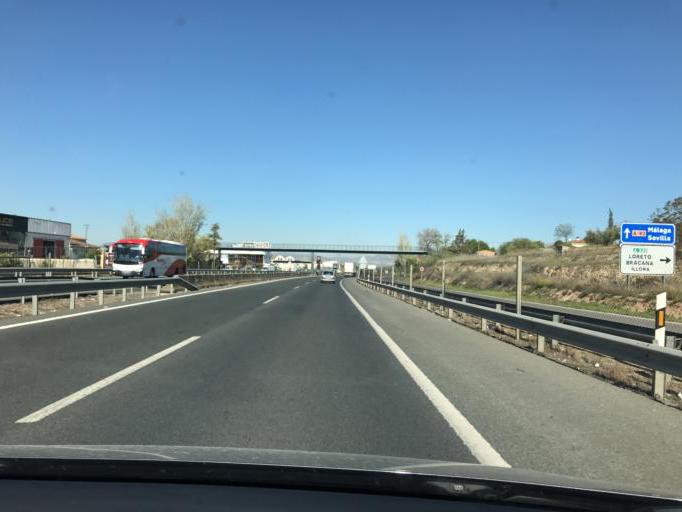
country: ES
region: Andalusia
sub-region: Provincia de Granada
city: Moraleda de Zafayona
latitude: 37.1841
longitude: -3.9557
